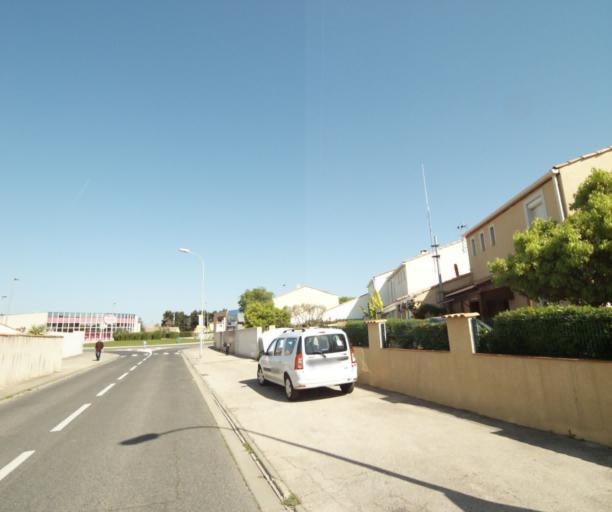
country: FR
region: Languedoc-Roussillon
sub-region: Departement de l'Herault
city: Lattes
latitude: 43.5756
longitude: 3.9127
